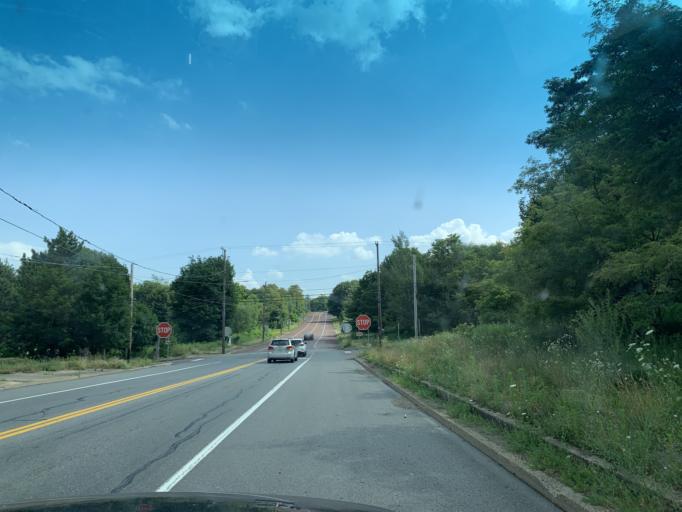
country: US
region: Pennsylvania
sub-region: Schuylkill County
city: Ashland
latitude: 40.8047
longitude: -76.3410
